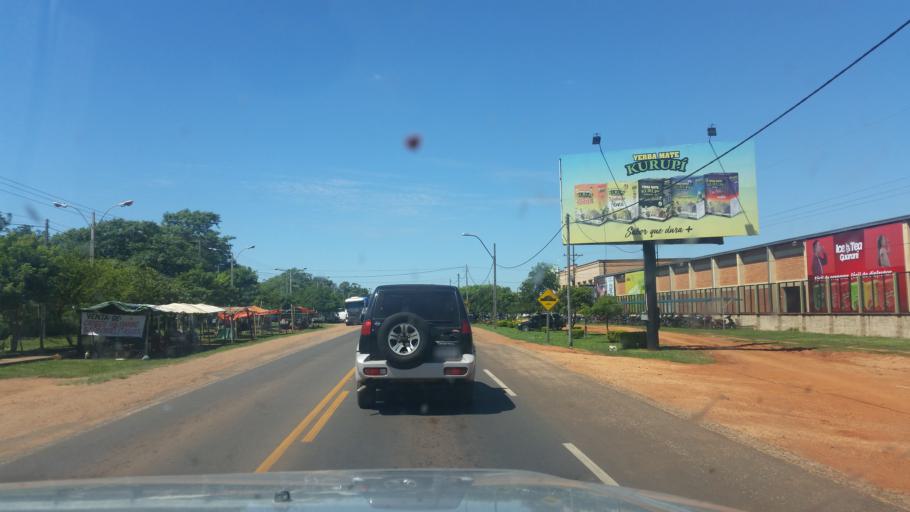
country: PY
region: Misiones
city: San Juan Bautista
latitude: -26.6730
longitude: -57.1202
